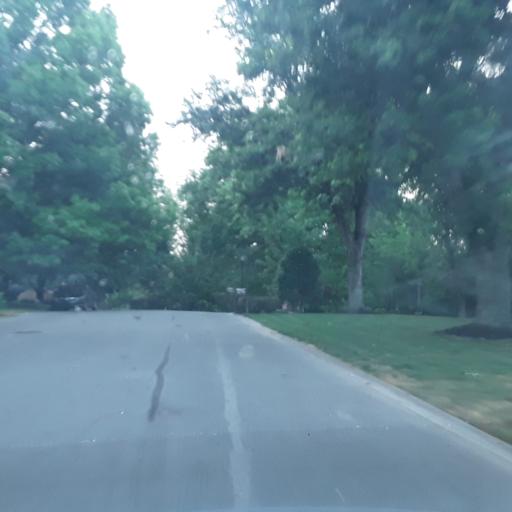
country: US
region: Tennessee
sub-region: Williamson County
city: Brentwood
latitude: 36.0470
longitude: -86.7605
